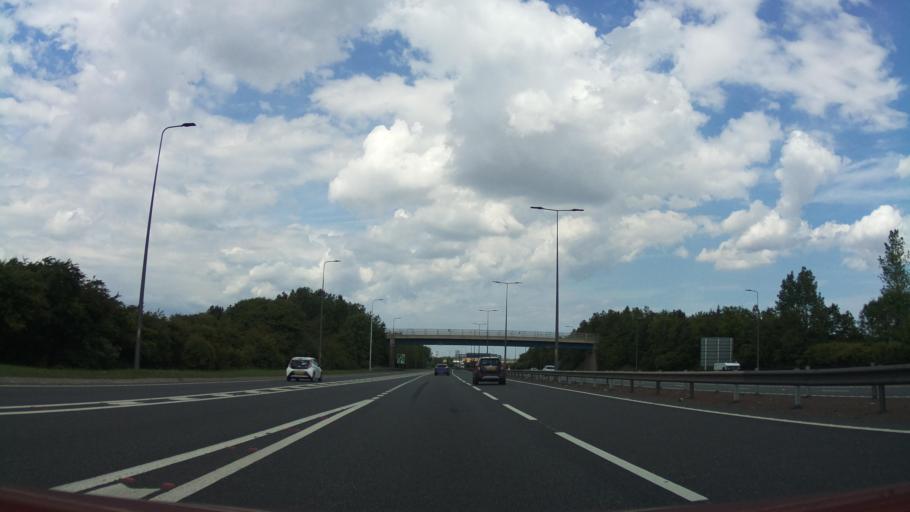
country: GB
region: England
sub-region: Redcar and Cleveland
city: Thornaby-on-Tees
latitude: 54.5320
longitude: -1.2801
